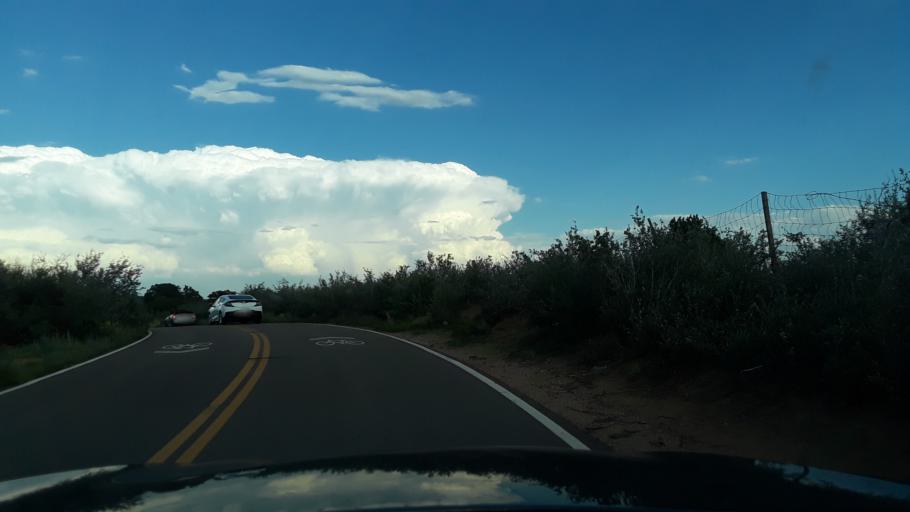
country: US
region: Colorado
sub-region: El Paso County
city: Colorado Springs
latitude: 38.8726
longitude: -104.7757
